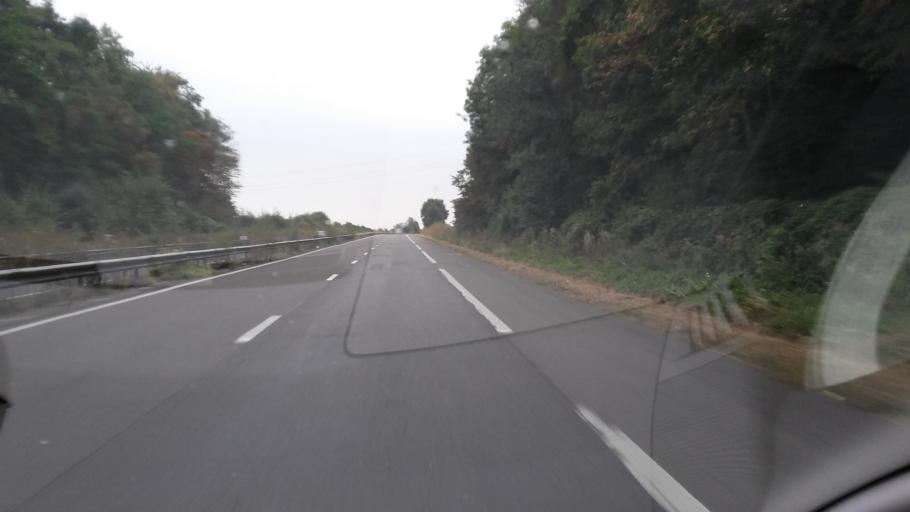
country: FR
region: Champagne-Ardenne
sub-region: Departement des Ardennes
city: Bazeilles
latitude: 49.6898
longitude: 4.9980
